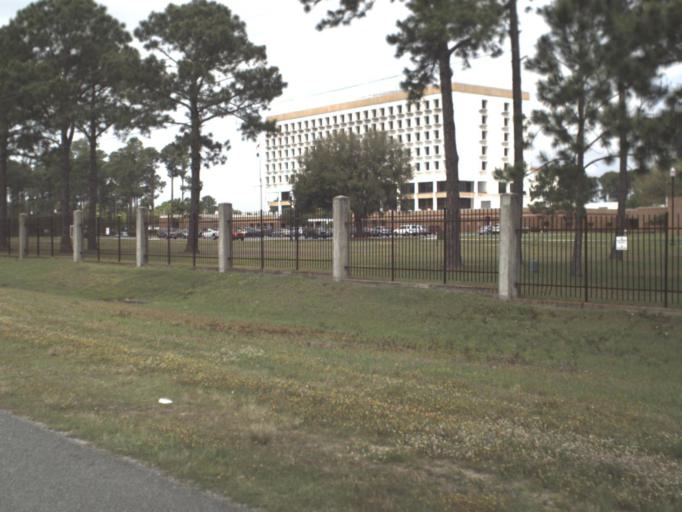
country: US
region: Florida
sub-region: Escambia County
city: Warrington
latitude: 30.3969
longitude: -87.2972
